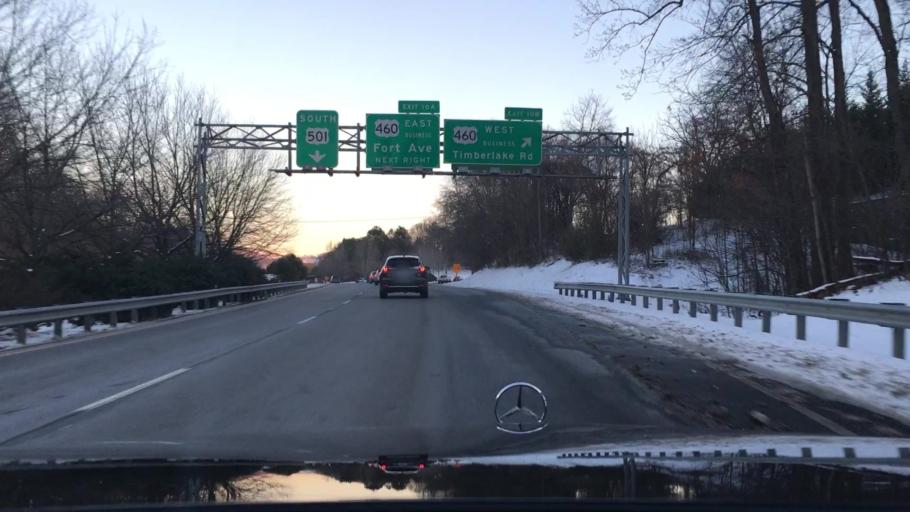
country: US
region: Virginia
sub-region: City of Lynchburg
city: West Lynchburg
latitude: 37.3684
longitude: -79.2086
